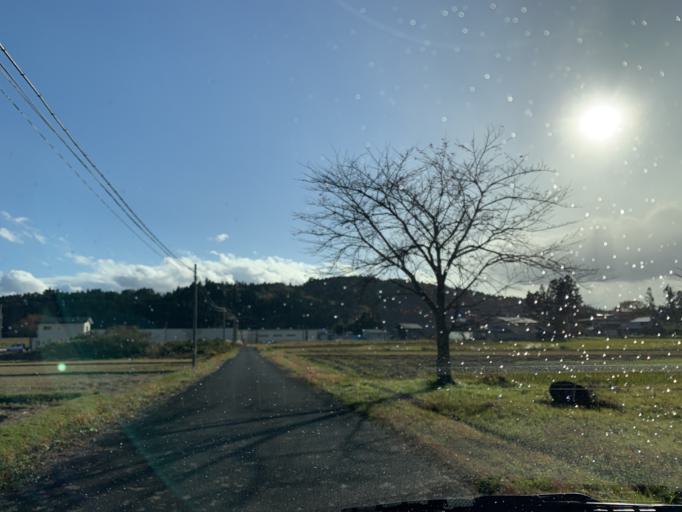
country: JP
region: Iwate
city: Ichinoseki
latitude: 39.0109
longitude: 141.1008
